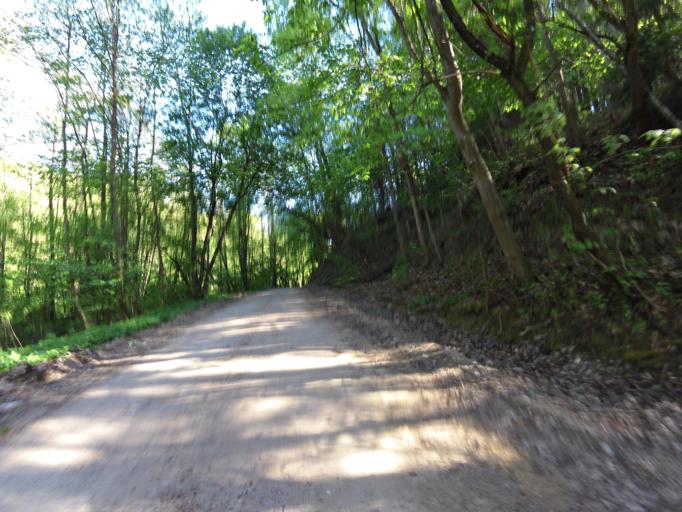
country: LT
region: Vilnius County
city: Pilaite
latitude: 54.6864
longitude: 25.1557
